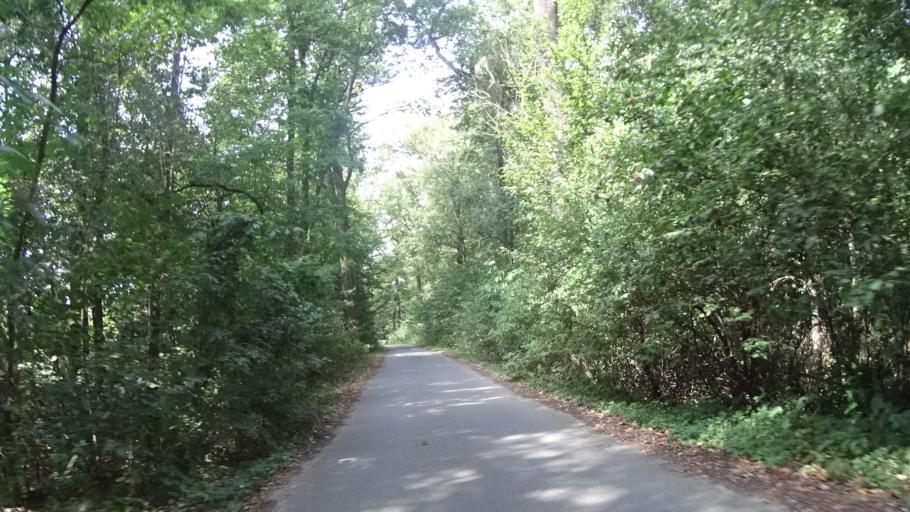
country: CZ
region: Olomoucky
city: Skrben
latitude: 49.6546
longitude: 17.1929
